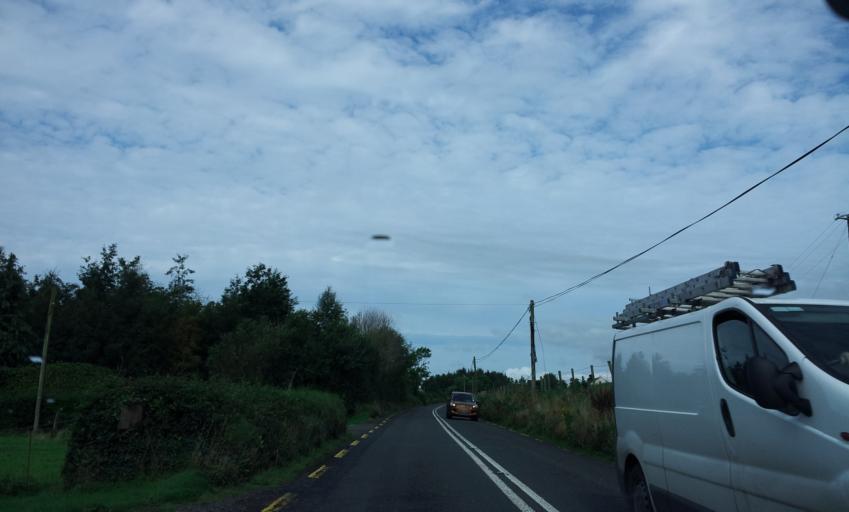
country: IE
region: Munster
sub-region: Ciarrai
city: Killorglin
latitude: 52.0763
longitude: -9.6546
